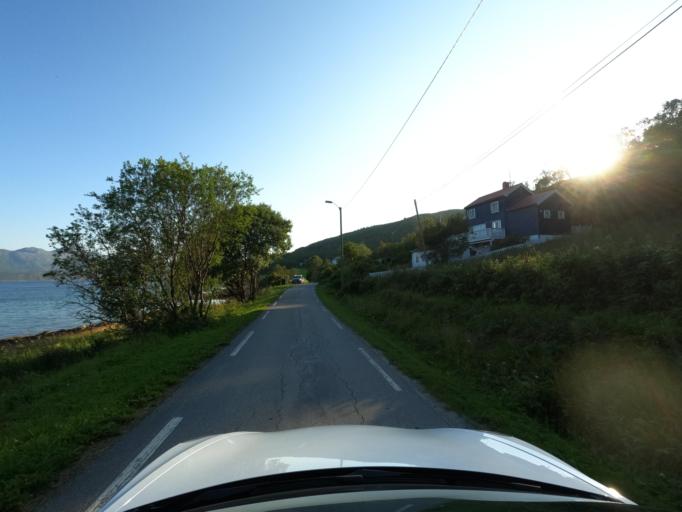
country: NO
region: Troms
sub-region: Skanland
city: Evenskjer
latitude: 68.4555
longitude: 16.5903
